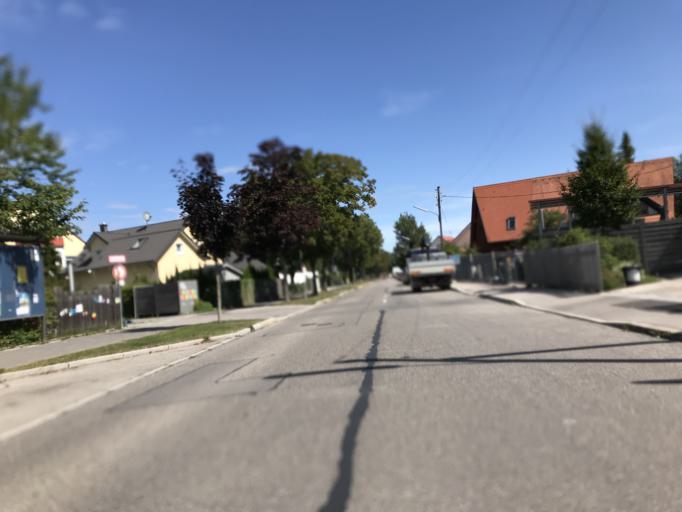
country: DE
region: Bavaria
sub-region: Upper Bavaria
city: Puchheim
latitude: 48.1748
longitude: 11.3516
